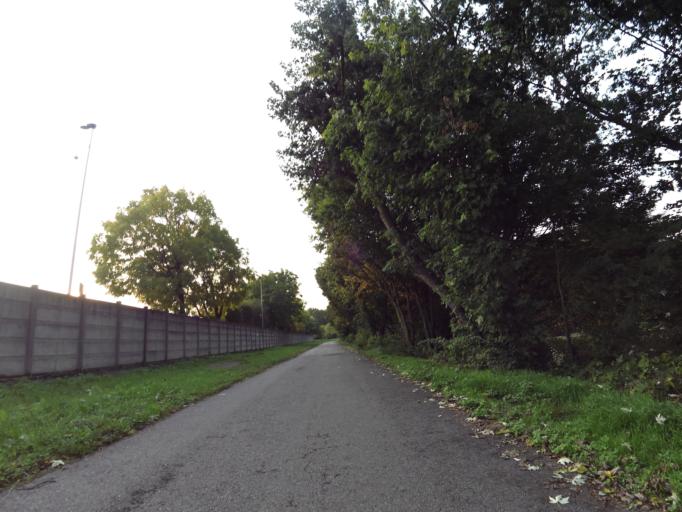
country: IT
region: Lombardy
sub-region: Citta metropolitana di Milano
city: San Donato Milanese
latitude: 45.4196
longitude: 9.2868
